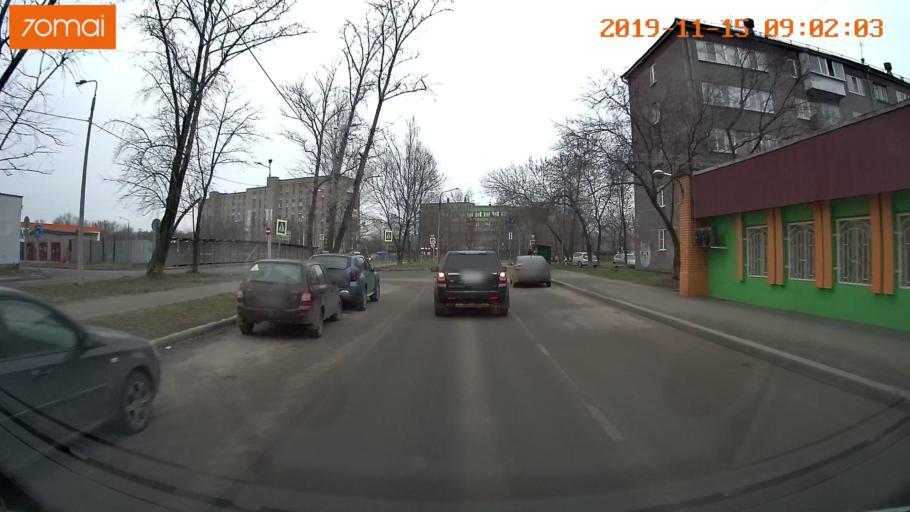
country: RU
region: Vologda
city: Cherepovets
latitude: 59.1354
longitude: 37.9271
